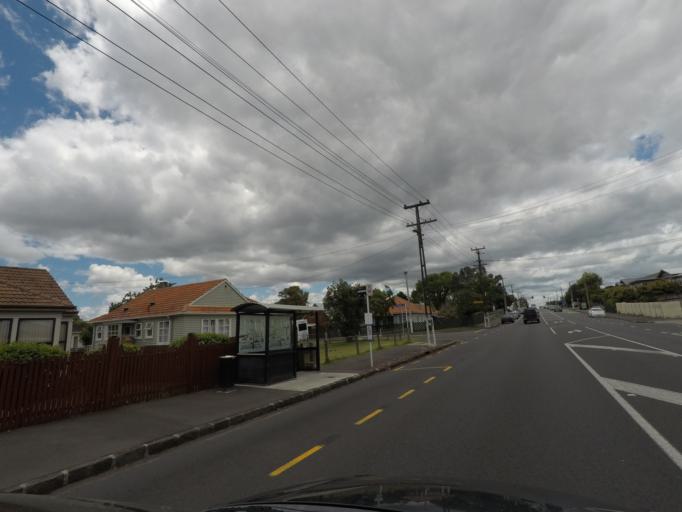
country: NZ
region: Auckland
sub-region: Auckland
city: Auckland
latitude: -36.8896
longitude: 174.7370
